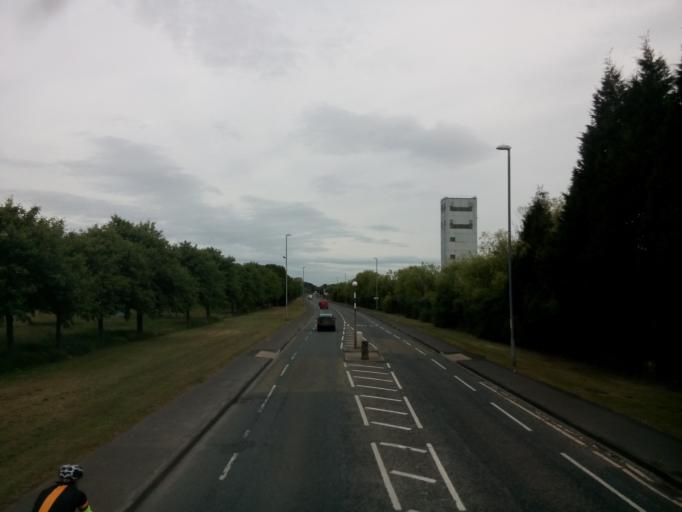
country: GB
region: England
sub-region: County Durham
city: Chester-le-Street
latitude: 54.8869
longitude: -1.5764
